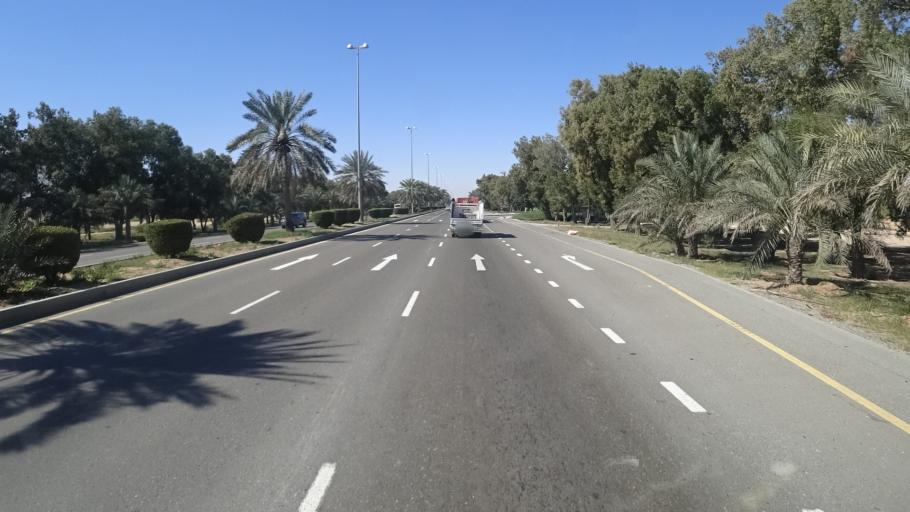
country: AE
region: Abu Dhabi
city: Al Ain
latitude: 24.0864
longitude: 55.6820
